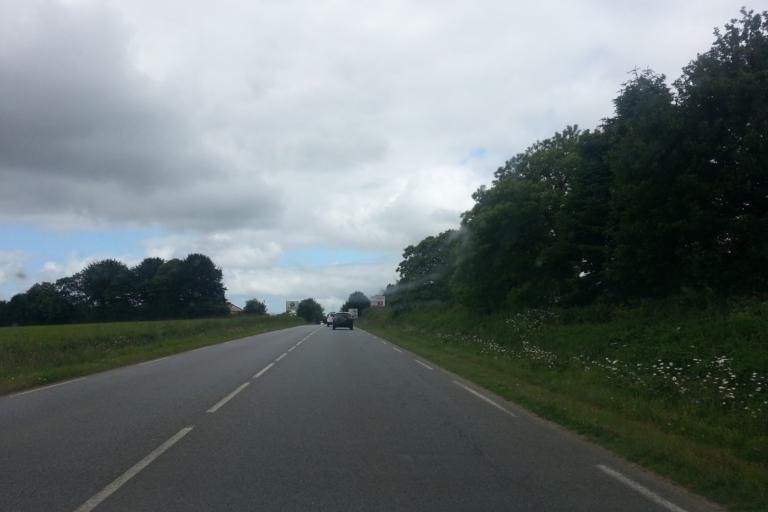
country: FR
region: Brittany
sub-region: Departement du Finistere
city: Briec
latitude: 48.0985
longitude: -4.0118
